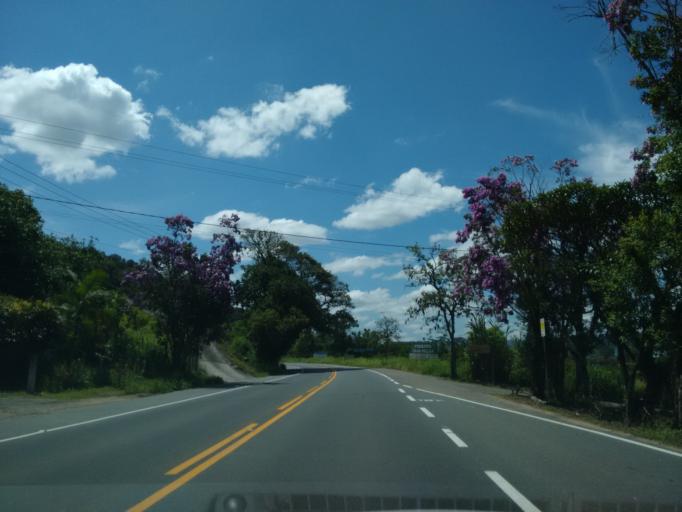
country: BR
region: Santa Catarina
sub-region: Pomerode
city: Pomerode
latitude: -26.7717
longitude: -49.1692
